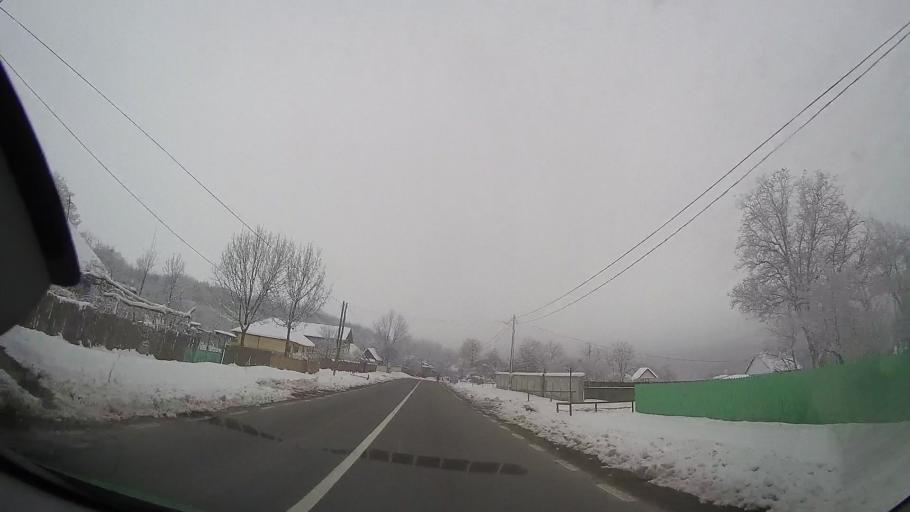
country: RO
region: Neamt
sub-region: Comuna Poenari
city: Poienari
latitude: 46.8844
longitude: 27.1318
